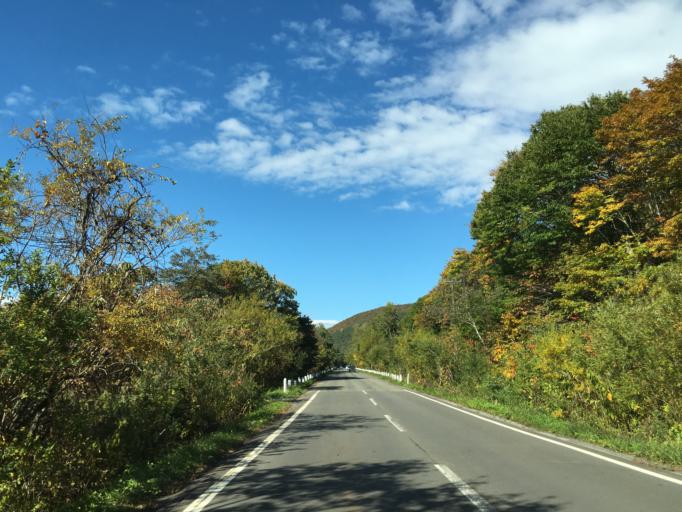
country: JP
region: Fukushima
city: Inawashiro
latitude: 37.5990
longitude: 140.2428
